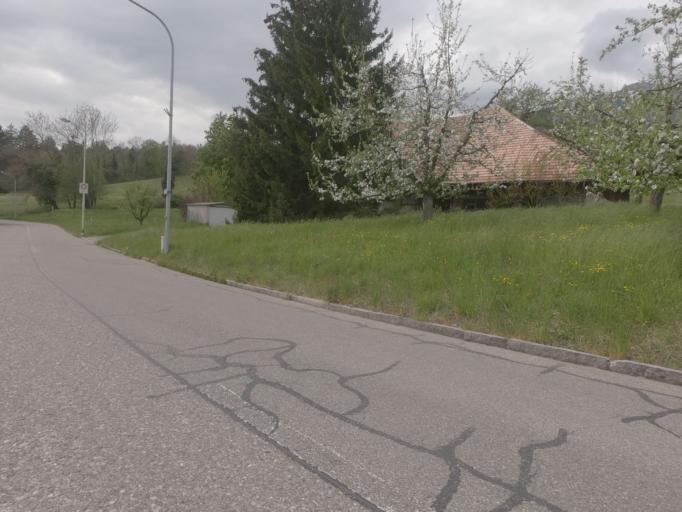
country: CH
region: Solothurn
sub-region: Bezirk Lebern
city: Riedholz
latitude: 47.2330
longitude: 7.5564
